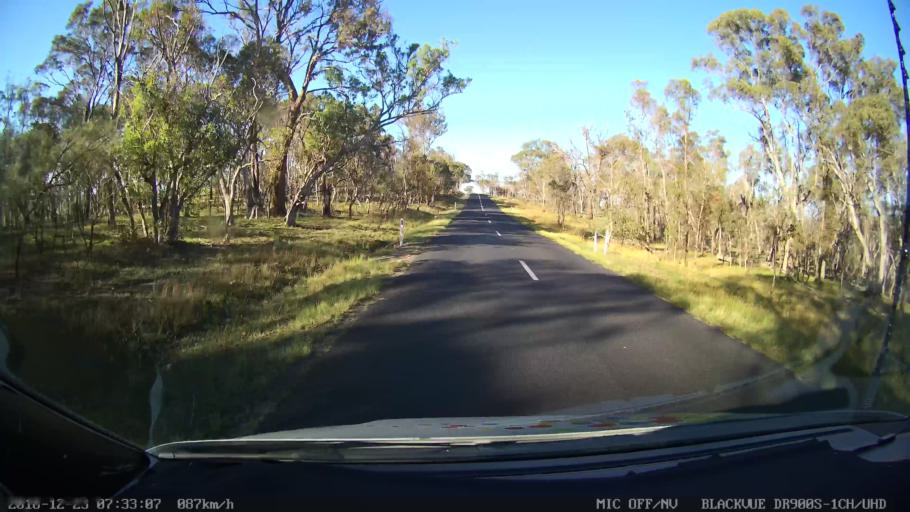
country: AU
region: New South Wales
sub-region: Armidale Dumaresq
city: Enmore
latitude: -30.5095
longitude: 152.1081
